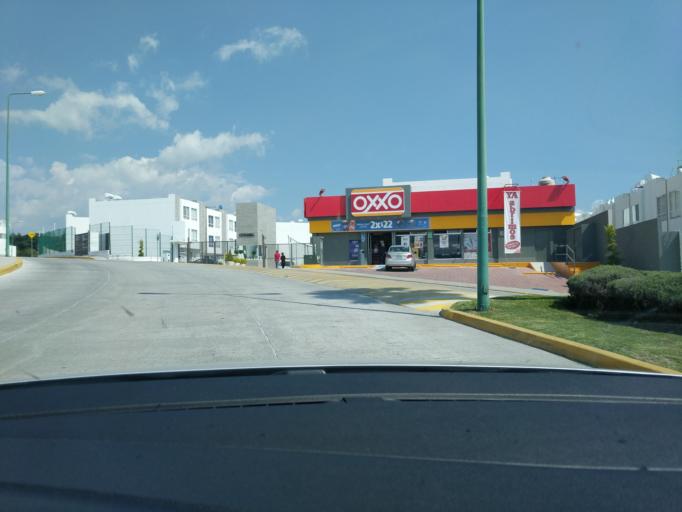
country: MX
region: Puebla
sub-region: Puebla
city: Galaxia la Calera
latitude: 19.0072
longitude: -98.1440
